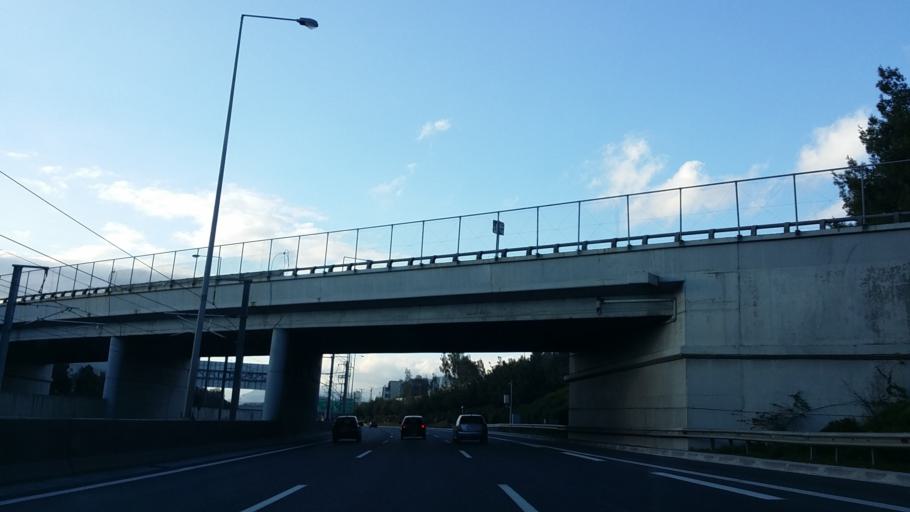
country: GR
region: Attica
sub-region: Nomarchia Athinas
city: Vrilissia
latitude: 38.0377
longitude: 23.8167
